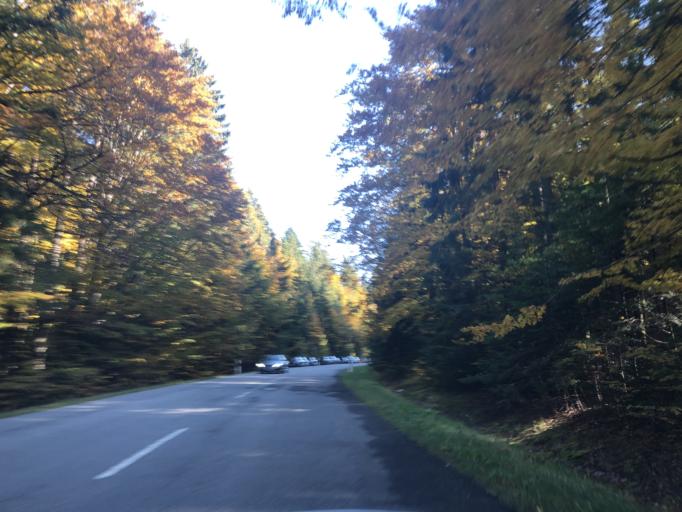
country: DE
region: Bavaria
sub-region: Lower Bavaria
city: Neuschonau
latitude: 48.8932
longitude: 13.4848
